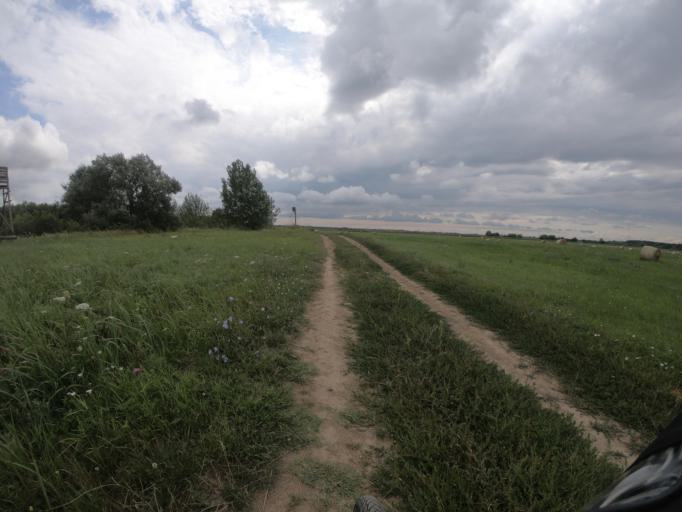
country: HU
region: Jasz-Nagykun-Szolnok
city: Tiszafured
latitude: 47.7094
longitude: 20.7782
